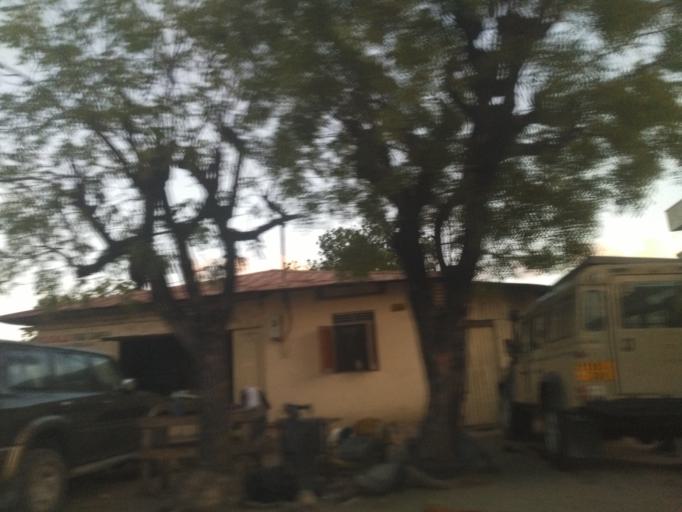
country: TZ
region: Dar es Salaam
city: Dar es Salaam
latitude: -6.8593
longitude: 39.2646
